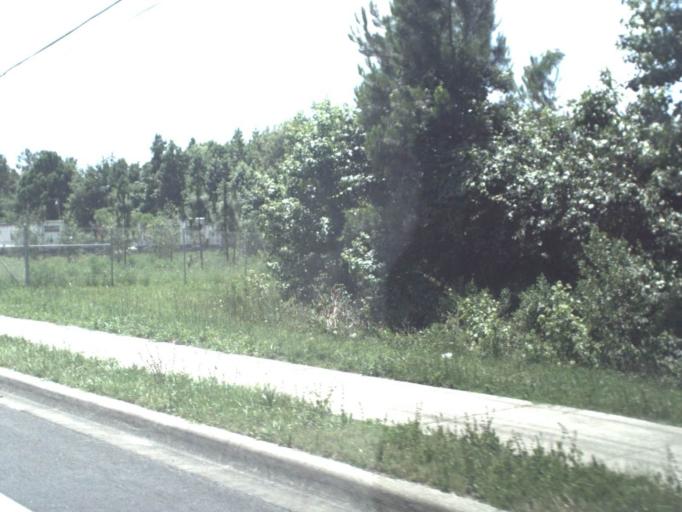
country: US
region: Florida
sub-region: Putnam County
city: Interlachen
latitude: 29.6288
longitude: -81.8275
